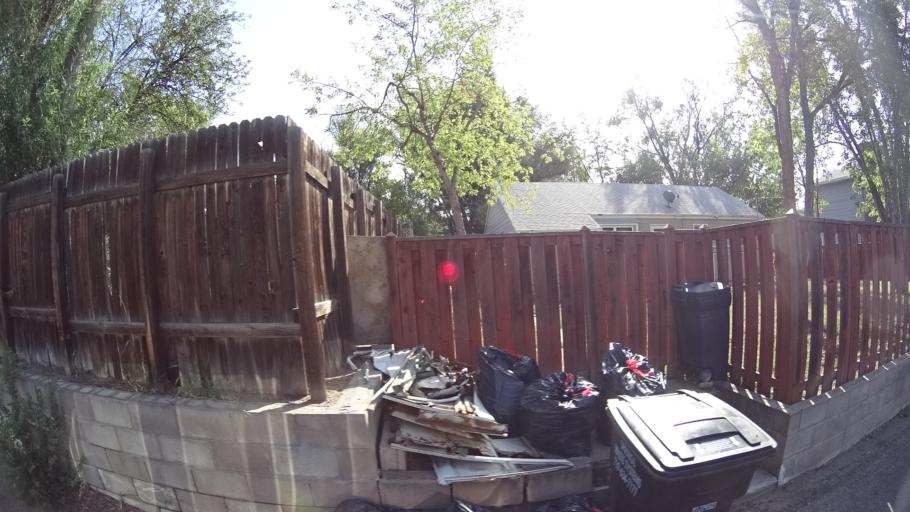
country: US
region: Colorado
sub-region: El Paso County
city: Colorado Springs
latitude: 38.8555
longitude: -104.7797
